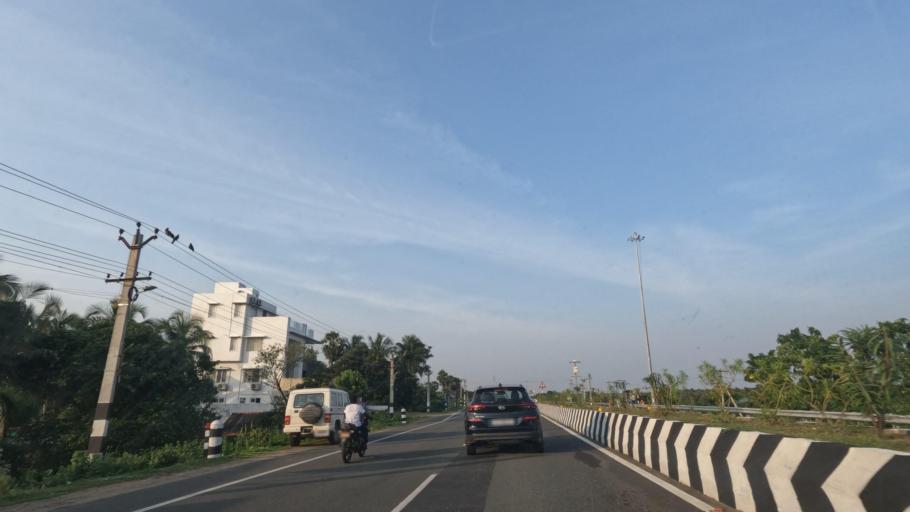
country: IN
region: Tamil Nadu
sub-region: Kancheepuram
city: Mamallapuram
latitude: 12.7179
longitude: 80.2278
